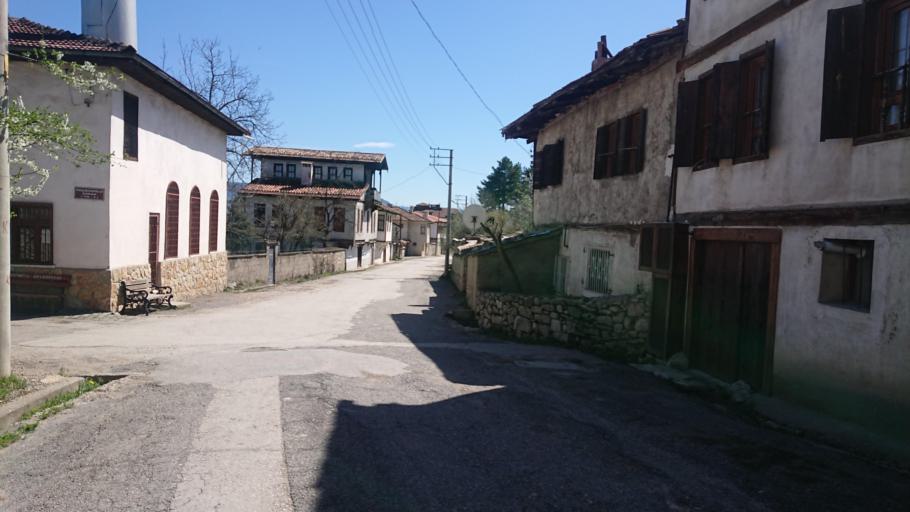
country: TR
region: Karabuk
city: Safranbolu
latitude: 41.2598
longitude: 32.6753
